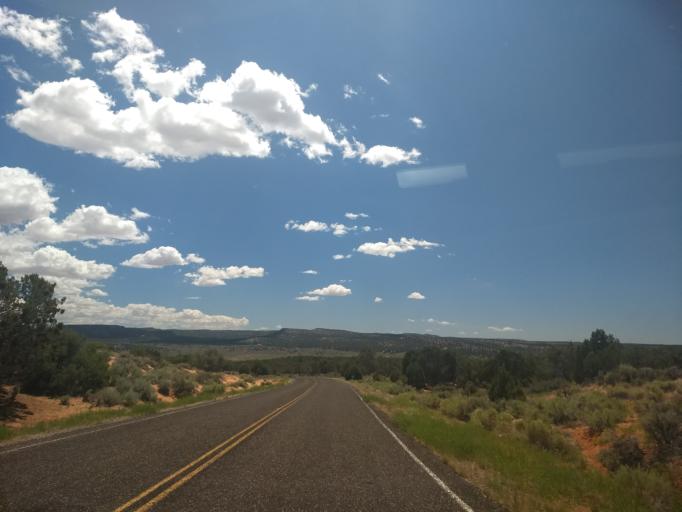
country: US
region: Utah
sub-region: Kane County
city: Kanab
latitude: 37.1782
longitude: -112.6576
